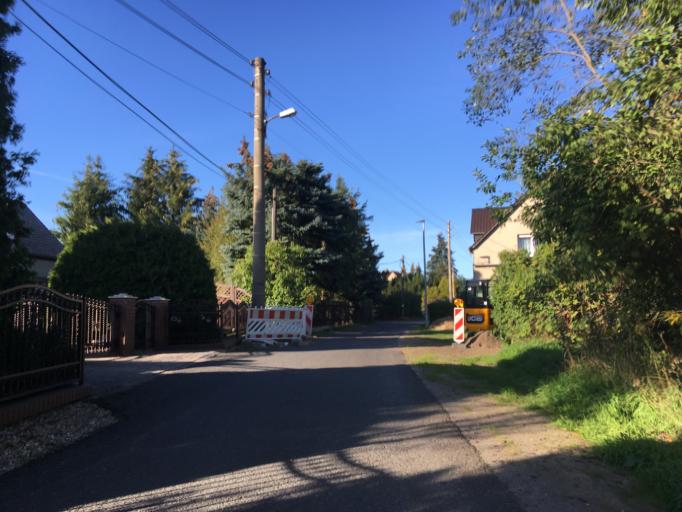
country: DE
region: Saxony
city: Bad Muskau
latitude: 51.5665
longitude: 14.7132
